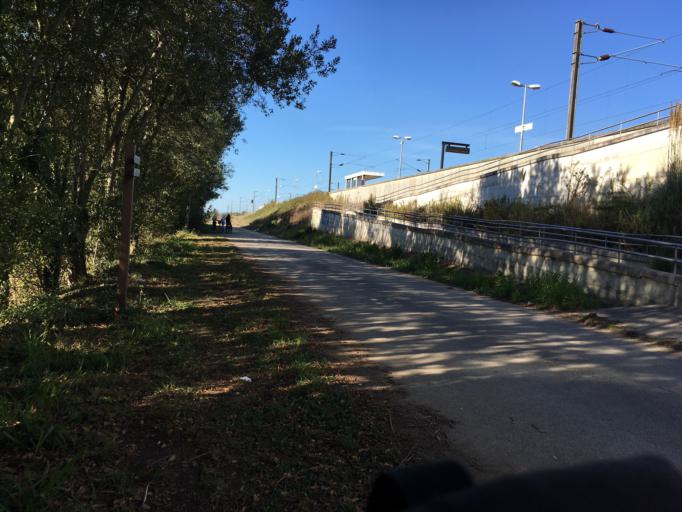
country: PT
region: Aveiro
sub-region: Estarreja
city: Salreu
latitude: 40.7158
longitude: -8.5641
